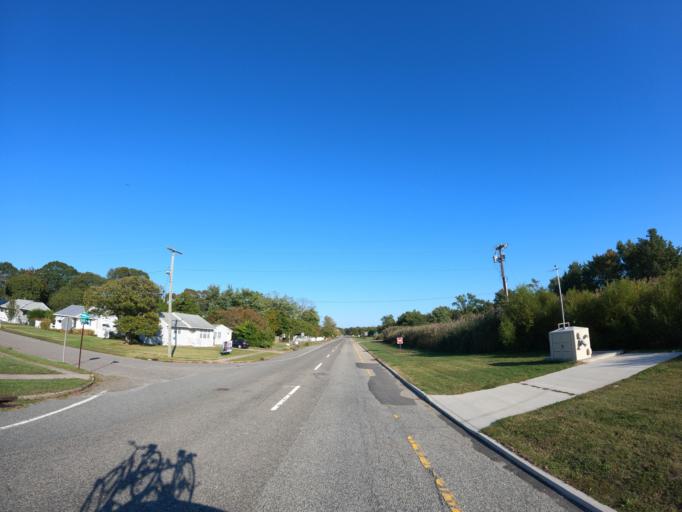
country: US
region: New Jersey
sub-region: Cape May County
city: North Cape May
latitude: 38.9734
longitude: -74.9492
